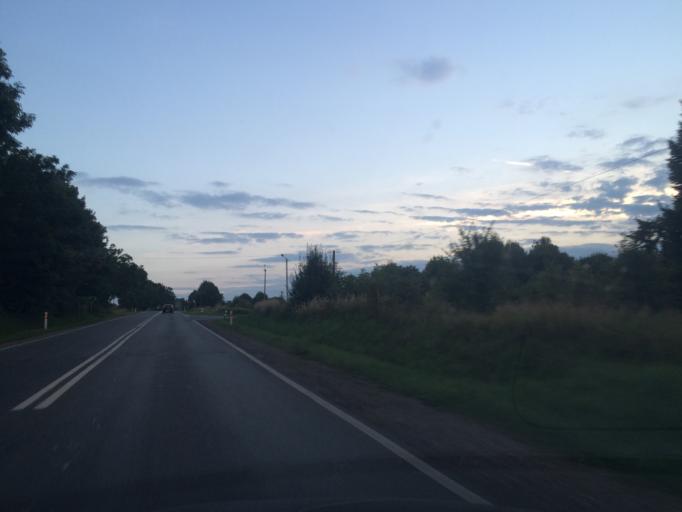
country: PL
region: Swietokrzyskie
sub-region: Powiat starachowicki
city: Wachock
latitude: 51.0719
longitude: 21.0021
